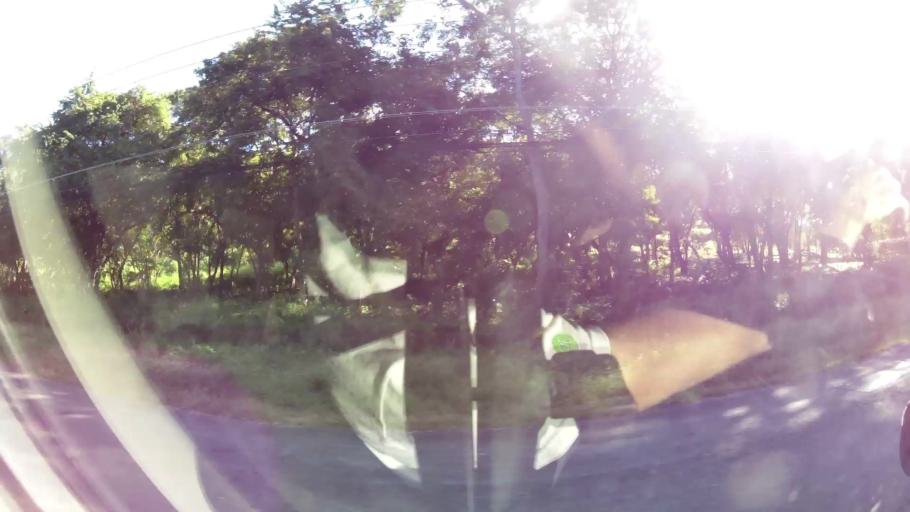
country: CR
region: Guanacaste
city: Sardinal
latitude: 10.5867
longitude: -85.6523
